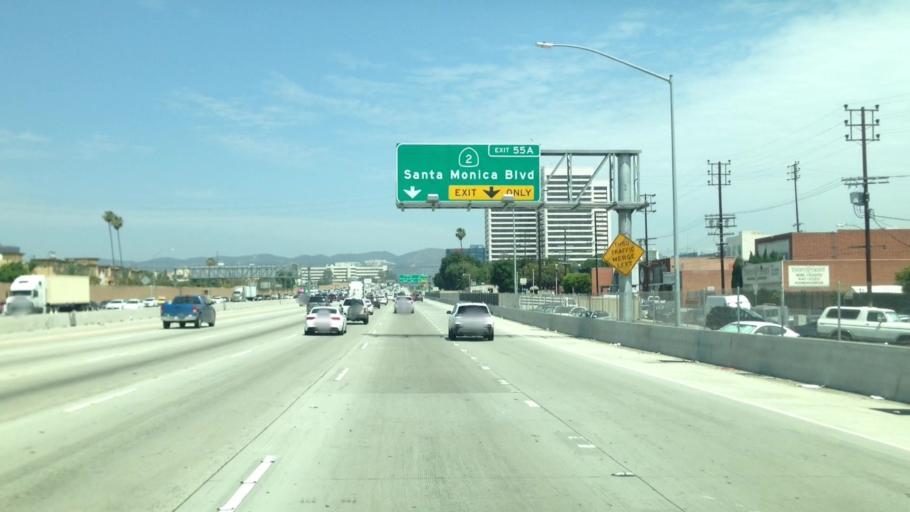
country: US
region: California
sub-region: Los Angeles County
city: Westwood, Los Angeles
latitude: 34.0407
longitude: -118.4410
